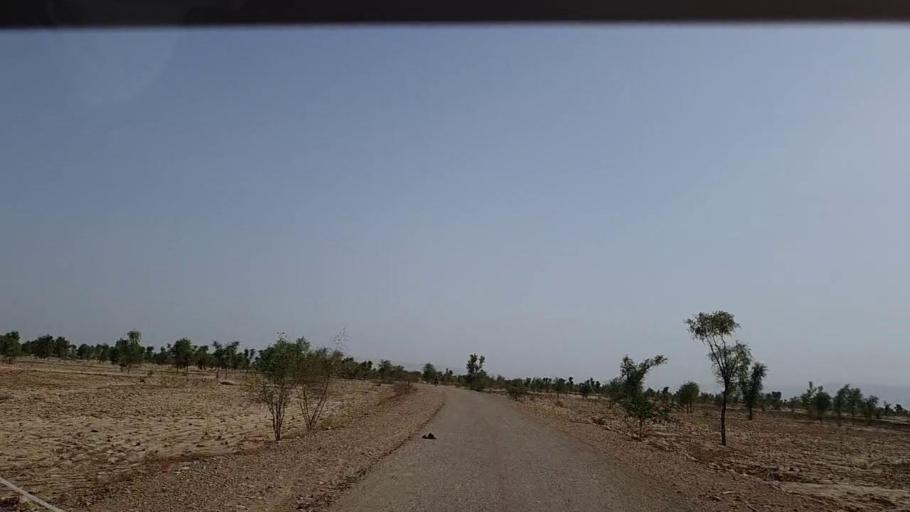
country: PK
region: Sindh
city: Johi
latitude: 26.6175
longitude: 67.4964
